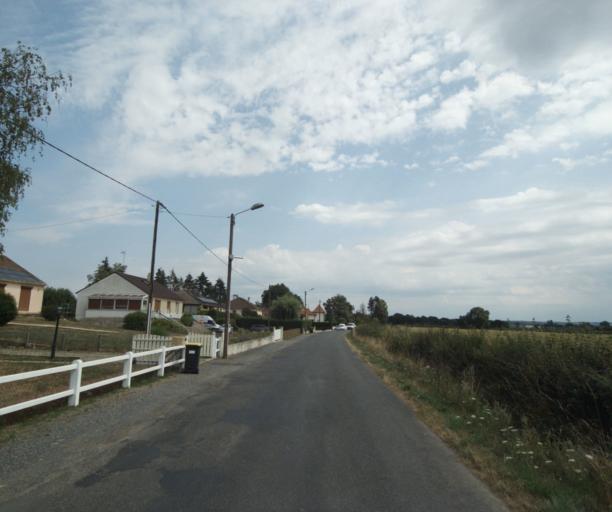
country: FR
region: Bourgogne
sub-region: Departement de Saone-et-Loire
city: Gueugnon
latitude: 46.6102
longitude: 4.0411
